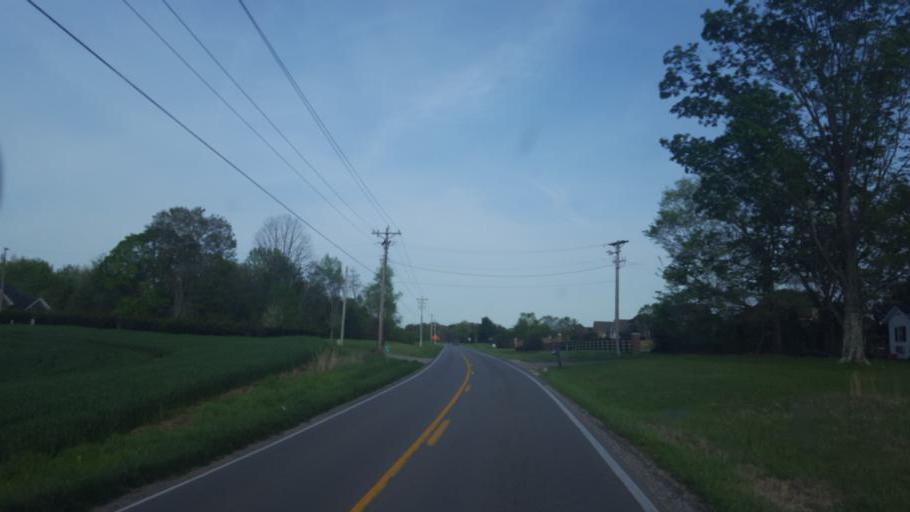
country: US
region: Kentucky
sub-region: Warren County
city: Bowling Green
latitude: 36.9650
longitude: -86.3731
